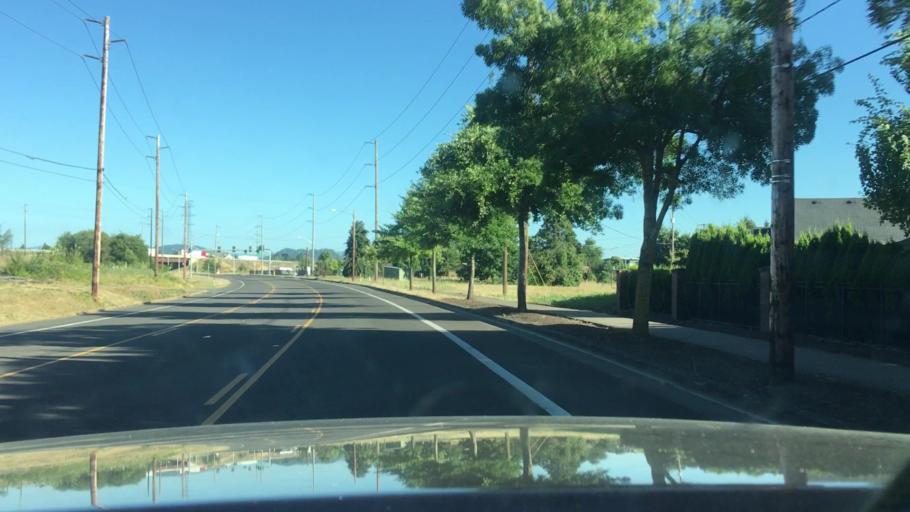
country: US
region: Oregon
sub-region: Lane County
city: Coburg
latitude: 44.0926
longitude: -123.0502
